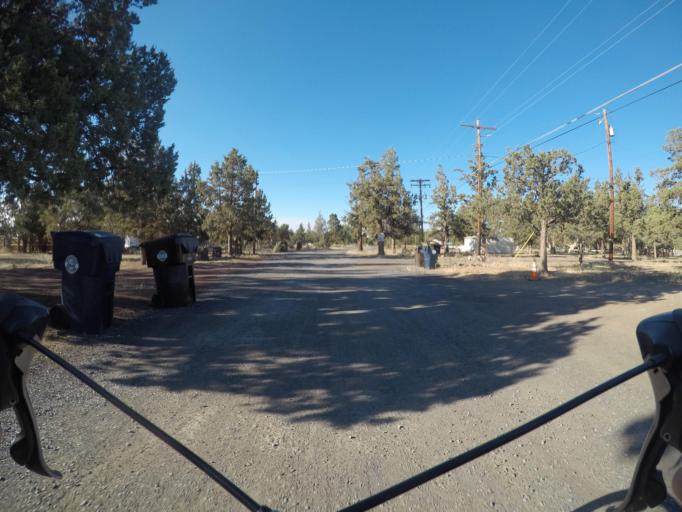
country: US
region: Oregon
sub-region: Deschutes County
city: Redmond
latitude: 44.2224
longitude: -121.2357
